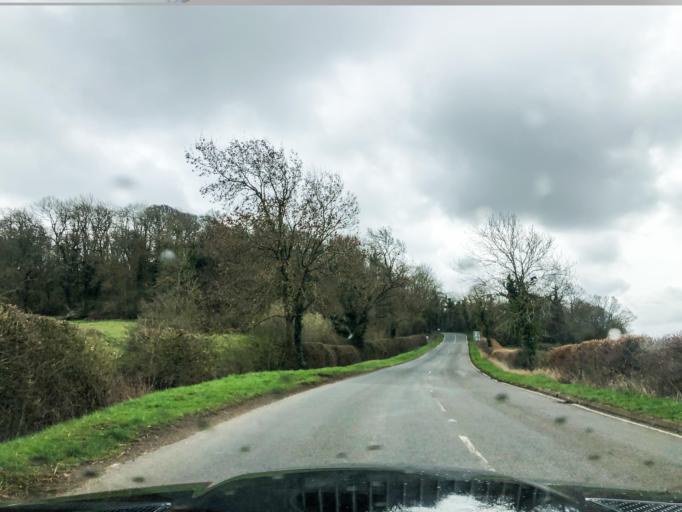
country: GB
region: England
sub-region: Oxfordshire
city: Hanwell
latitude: 52.1361
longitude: -1.4460
